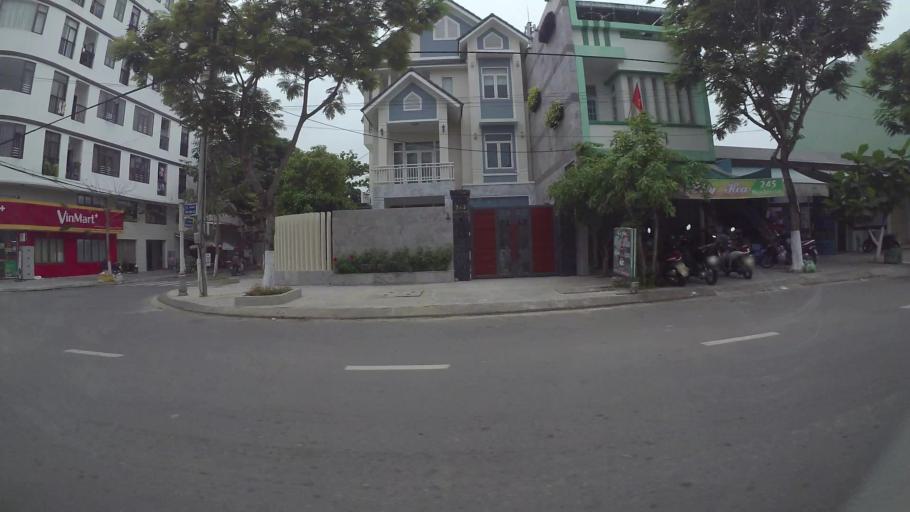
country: VN
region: Da Nang
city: Cam Le
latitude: 16.0371
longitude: 108.2091
